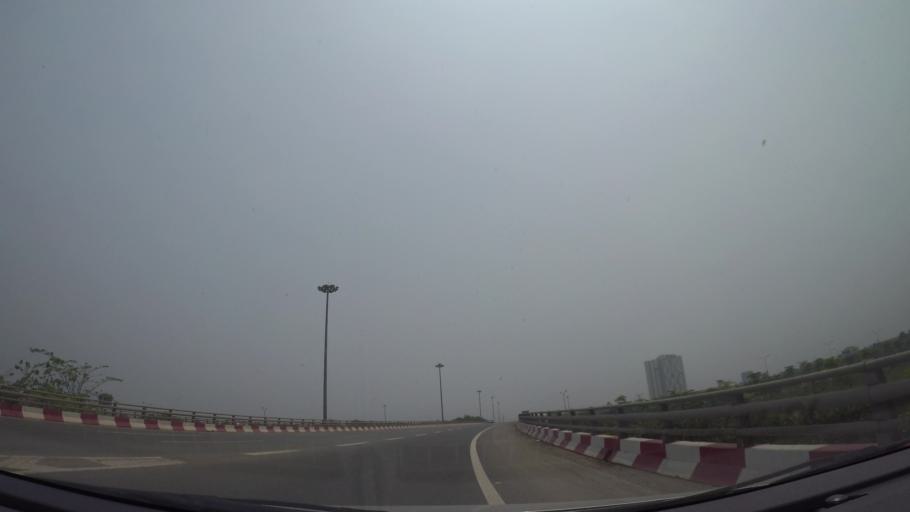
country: VN
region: Ha Noi
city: Lien Quan
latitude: 20.9902
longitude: 105.5243
